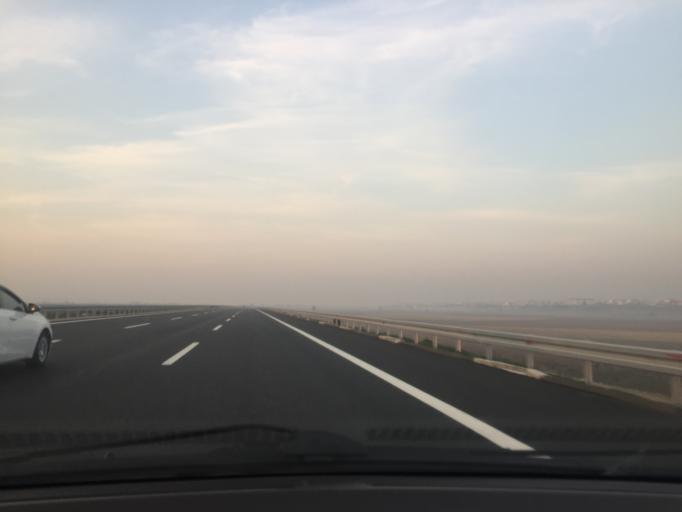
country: TR
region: Bursa
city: Karacabey
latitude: 40.2193
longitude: 28.3985
